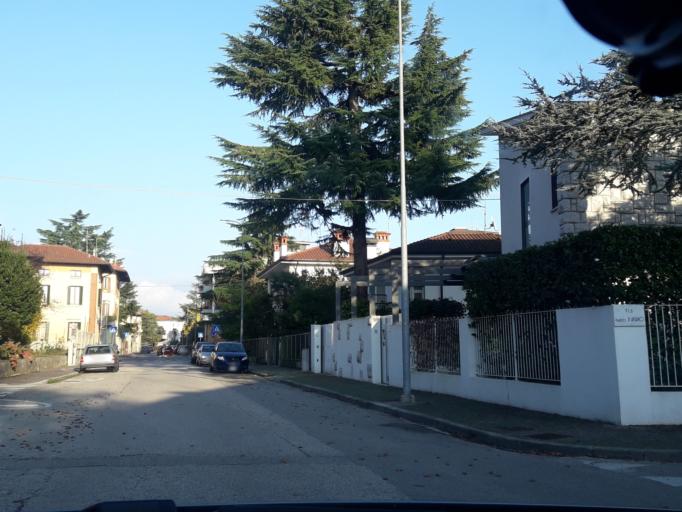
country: IT
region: Friuli Venezia Giulia
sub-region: Provincia di Udine
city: Udine
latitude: 46.0756
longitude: 13.2363
